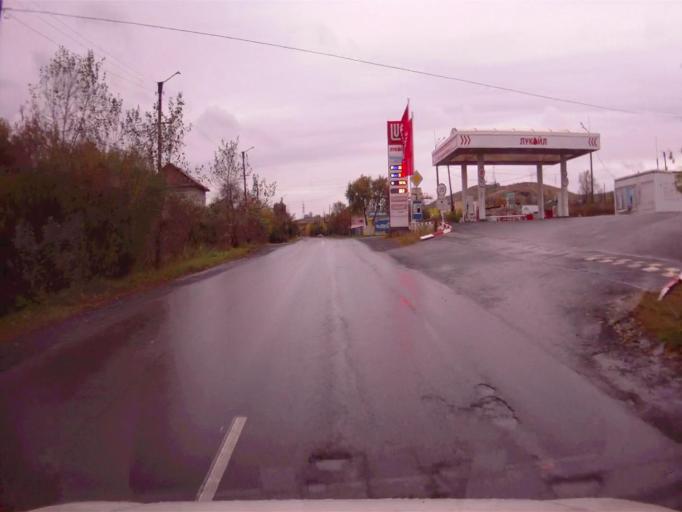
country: RU
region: Chelyabinsk
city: Verkhniy Ufaley
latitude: 56.0504
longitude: 60.2453
